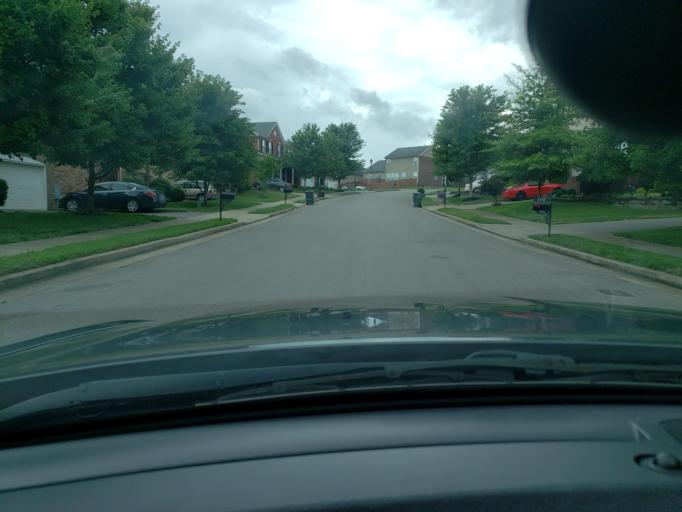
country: US
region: Tennessee
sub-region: Williamson County
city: Nolensville
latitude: 36.0228
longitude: -86.6983
